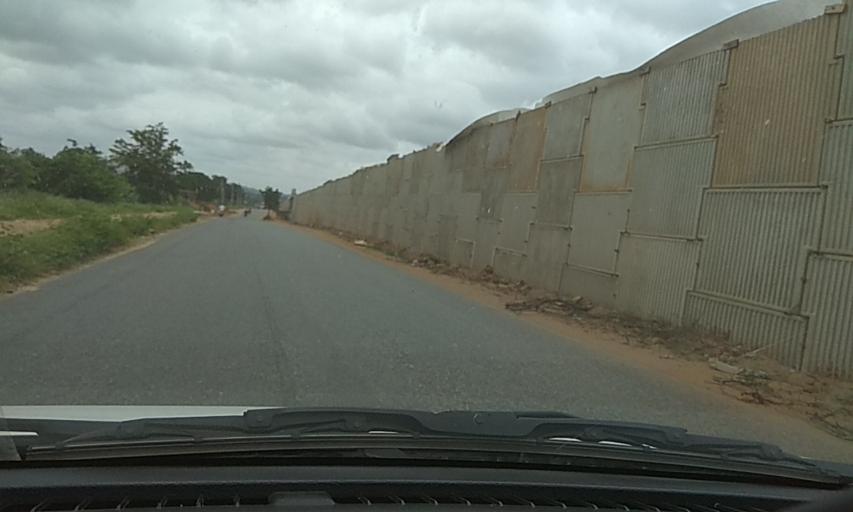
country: IN
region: Karnataka
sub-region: Chitradurga
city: Chitradurga
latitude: 14.2831
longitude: 76.3027
